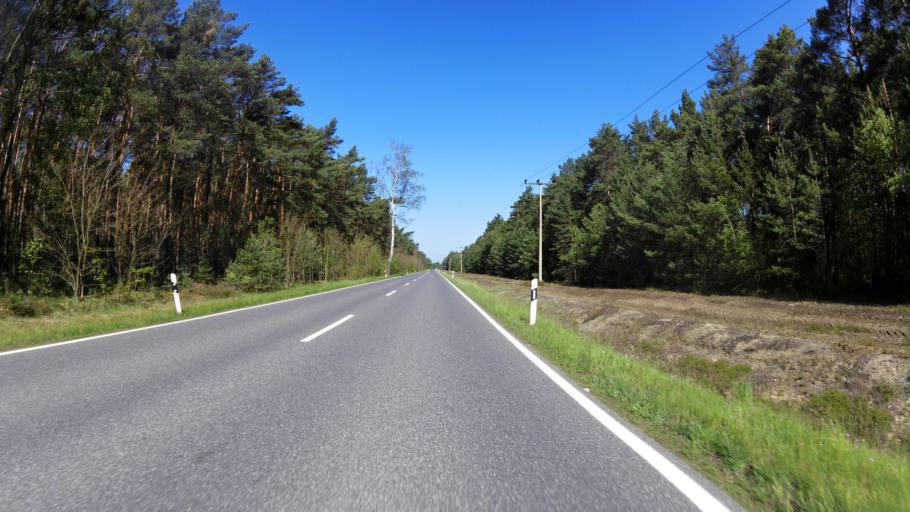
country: DE
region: Brandenburg
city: Guteborn
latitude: 51.4107
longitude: 13.9546
